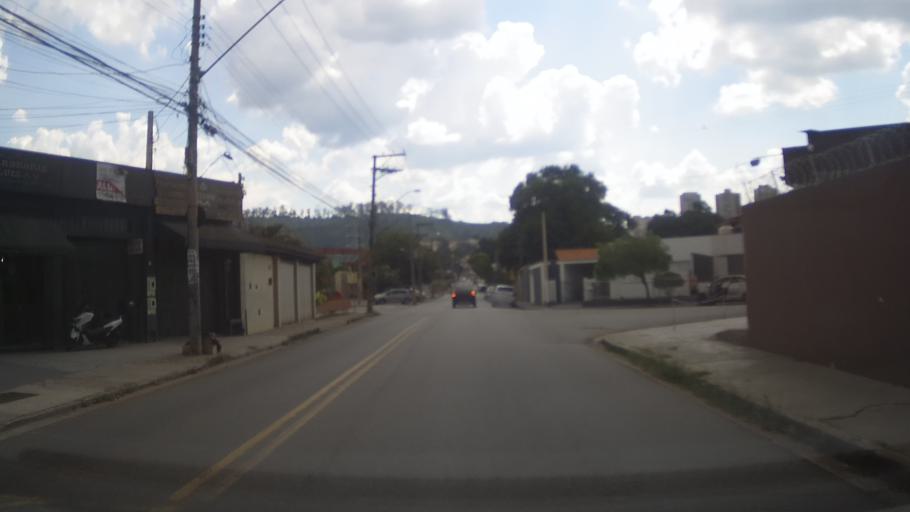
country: BR
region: Sao Paulo
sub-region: Jundiai
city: Jundiai
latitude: -23.2047
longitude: -46.8817
